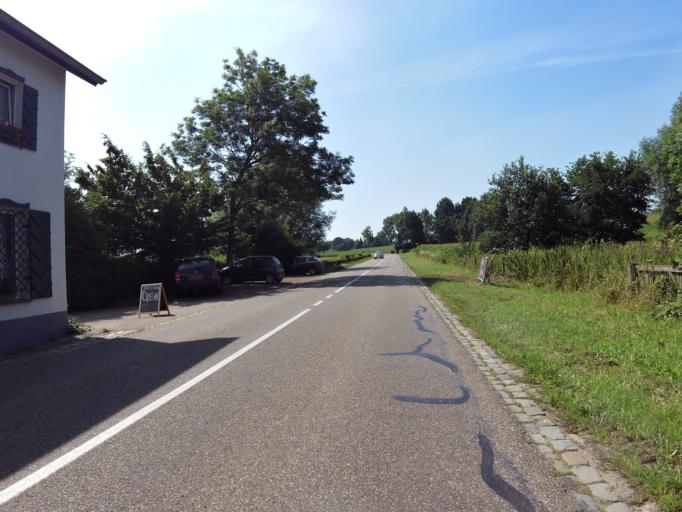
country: BE
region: Wallonia
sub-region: Province de Liege
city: Plombieres
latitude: 50.7839
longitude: 5.9188
